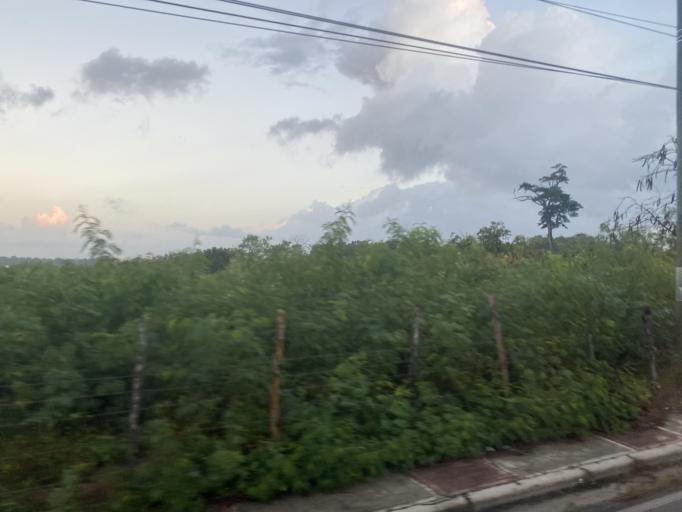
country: DO
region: San Juan
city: Punta Cana
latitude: 18.7075
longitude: -68.4644
